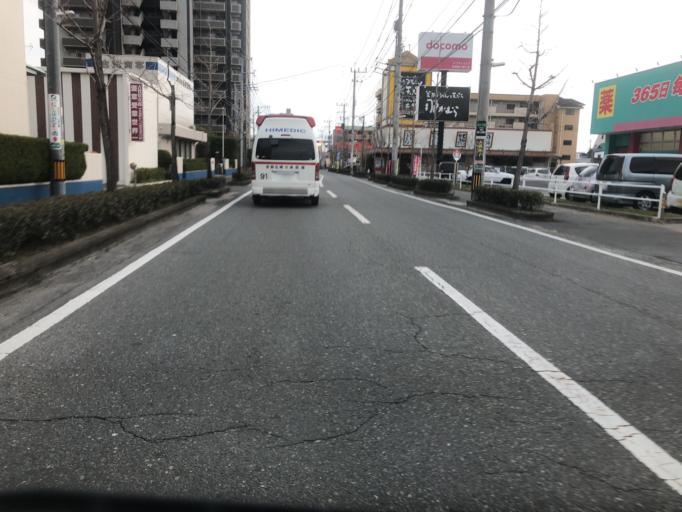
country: JP
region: Saga Prefecture
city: Saga-shi
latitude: 33.2791
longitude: 130.2699
